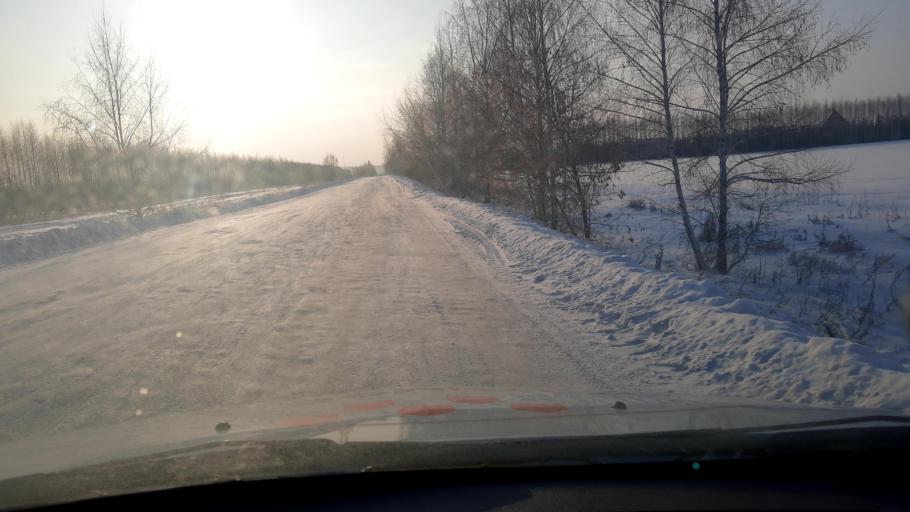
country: RU
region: Bashkortostan
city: Iglino
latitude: 54.7524
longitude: 56.2864
